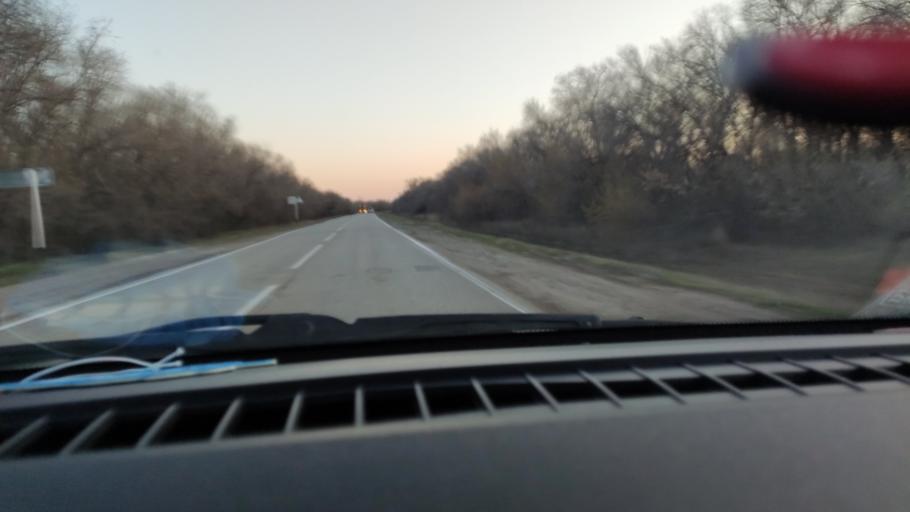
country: RU
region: Saratov
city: Privolzhskiy
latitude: 51.2441
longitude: 45.9337
